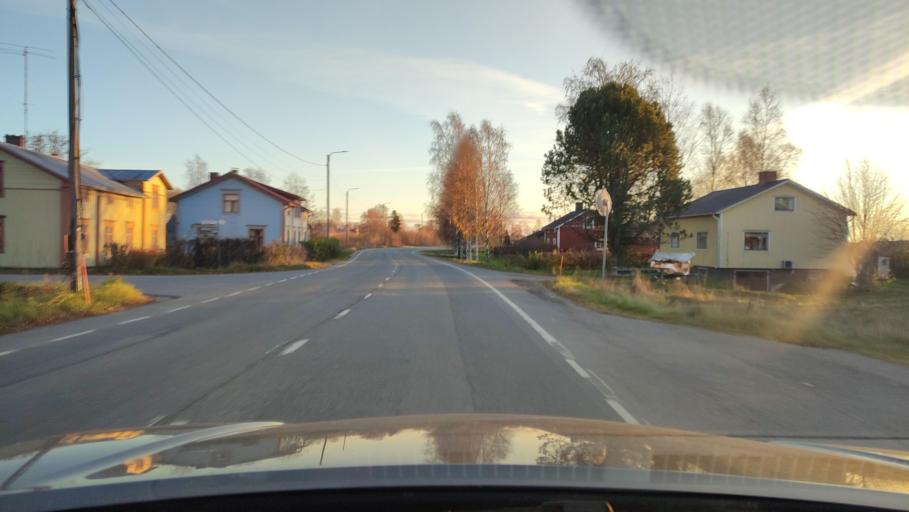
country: FI
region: Ostrobothnia
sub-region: Sydosterbotten
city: Naerpes
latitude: 62.4670
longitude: 21.3556
